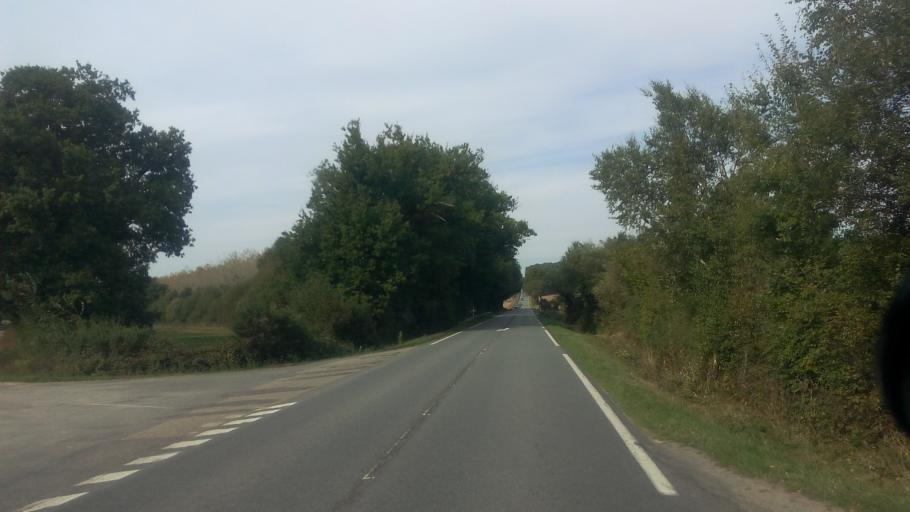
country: FR
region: Brittany
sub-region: Departement d'Ille-et-Vilaine
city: Bains-sur-Oust
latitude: 47.7179
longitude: -2.0941
